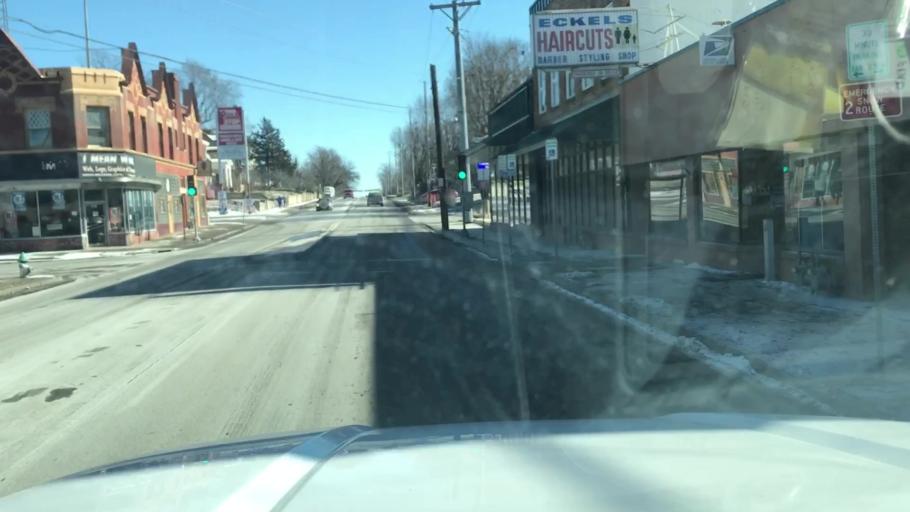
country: US
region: Missouri
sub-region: Buchanan County
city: Saint Joseph
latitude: 39.7768
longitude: -94.8299
